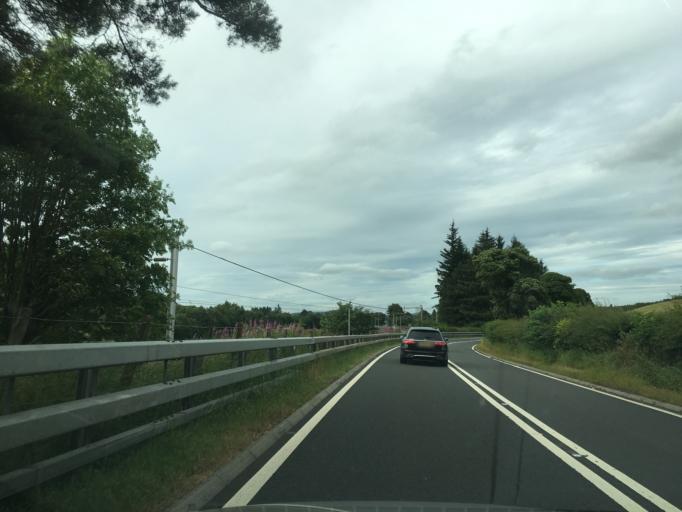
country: GB
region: Scotland
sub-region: South Lanarkshire
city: Biggar
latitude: 55.5514
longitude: -3.6380
